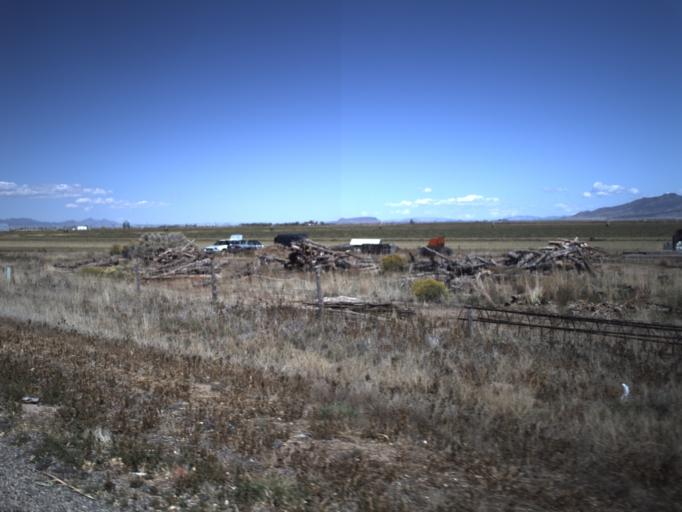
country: US
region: Utah
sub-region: Washington County
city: Enterprise
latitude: 37.6500
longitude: -113.6612
